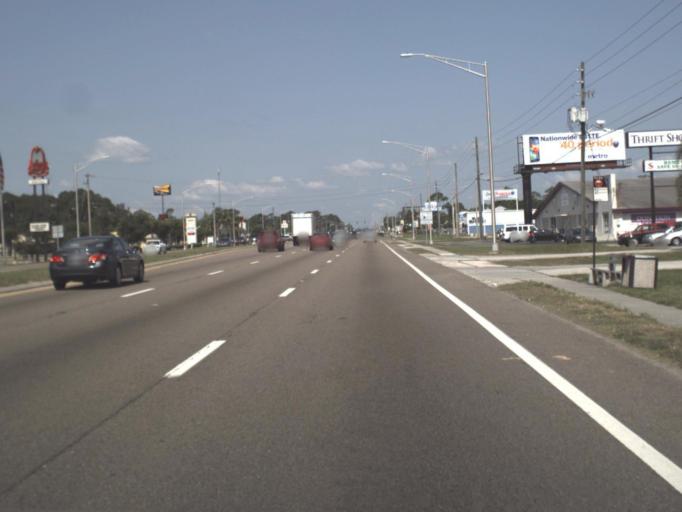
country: US
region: Florida
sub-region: Duval County
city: Neptune Beach
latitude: 30.2870
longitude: -81.5287
